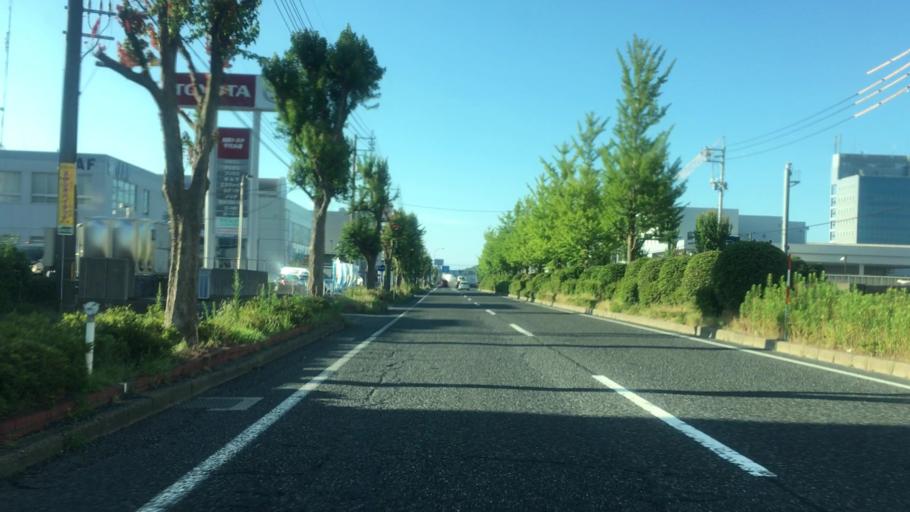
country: JP
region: Tottori
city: Tottori
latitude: 35.5143
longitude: 134.2020
